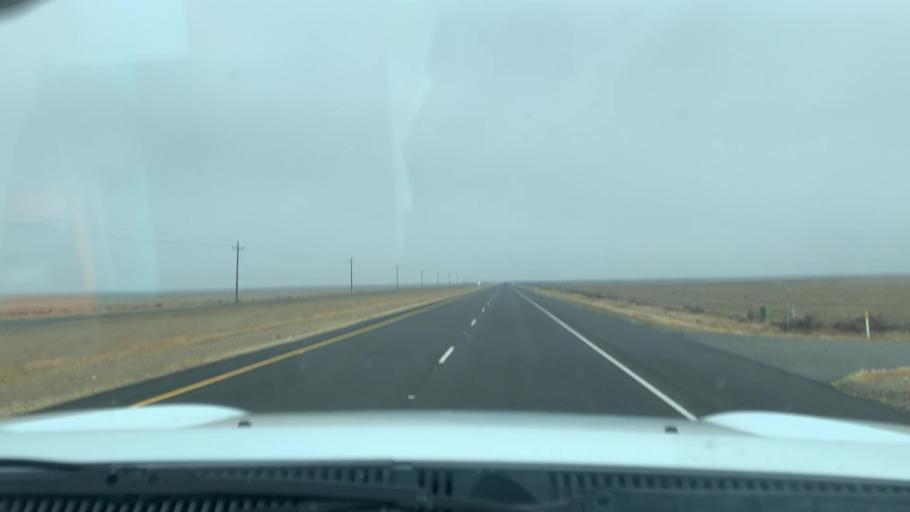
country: US
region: California
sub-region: Kern County
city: Lost Hills
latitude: 35.6154
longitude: -119.8233
